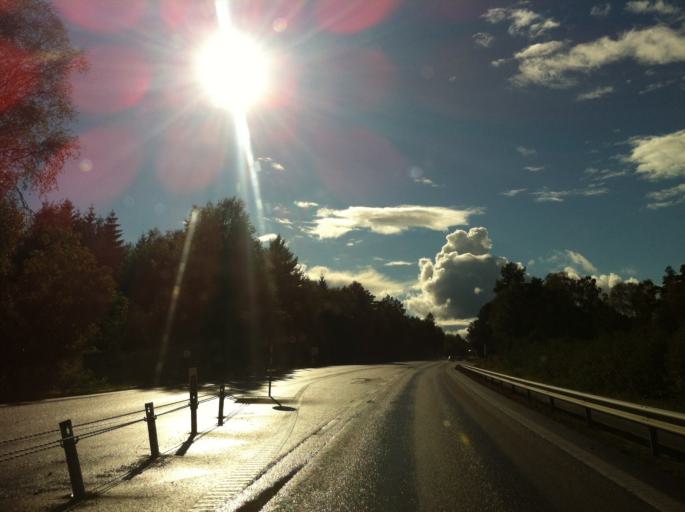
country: SE
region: Skane
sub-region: Perstorps Kommun
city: Perstorp
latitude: 56.1426
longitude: 13.5297
